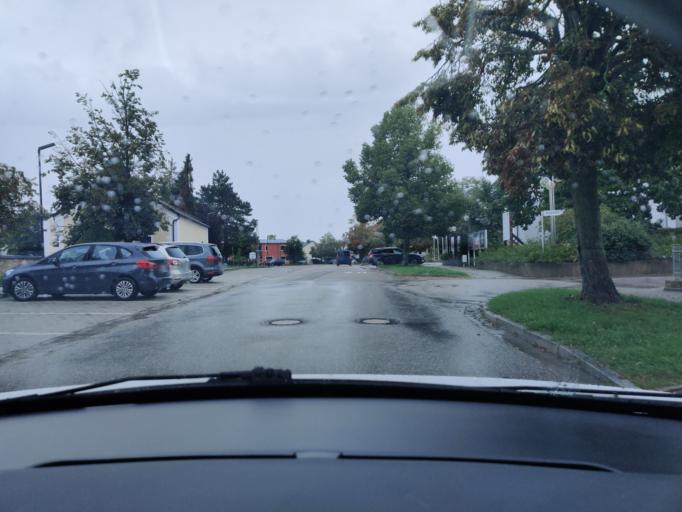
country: DE
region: Bavaria
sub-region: Upper Palatinate
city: Schwarzenfeld
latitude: 49.3886
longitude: 12.1360
